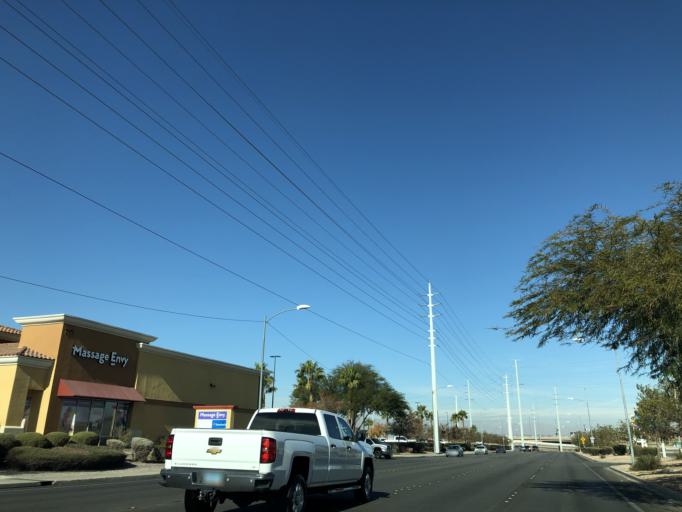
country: US
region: Nevada
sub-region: Clark County
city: Whitney
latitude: 36.0672
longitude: -115.0362
